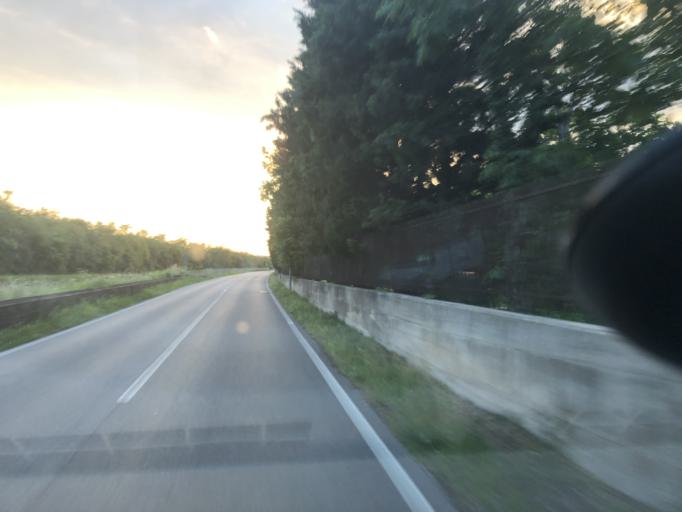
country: IT
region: Veneto
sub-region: Provincia di Verona
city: San Vito al Mantico
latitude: 45.4719
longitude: 10.8790
